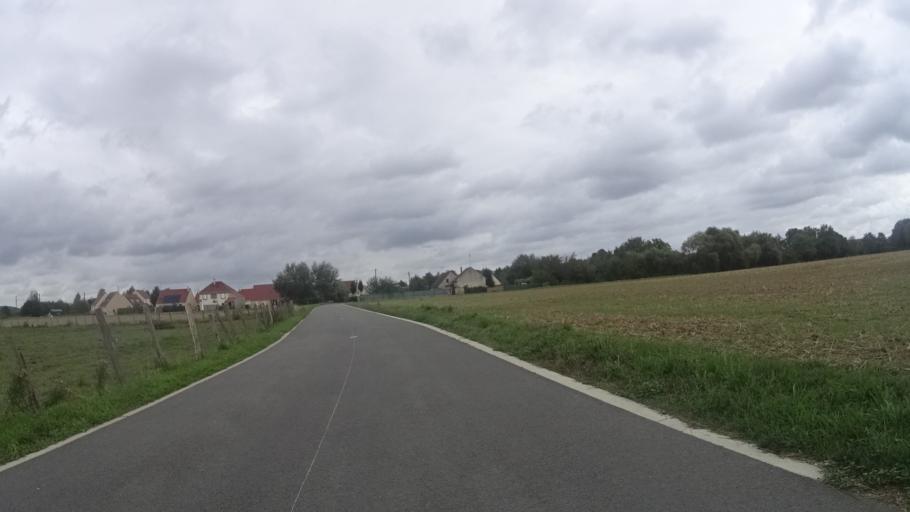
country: FR
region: Picardie
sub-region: Departement de l'Oise
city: Dreslincourt
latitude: 49.5116
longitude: 2.9448
